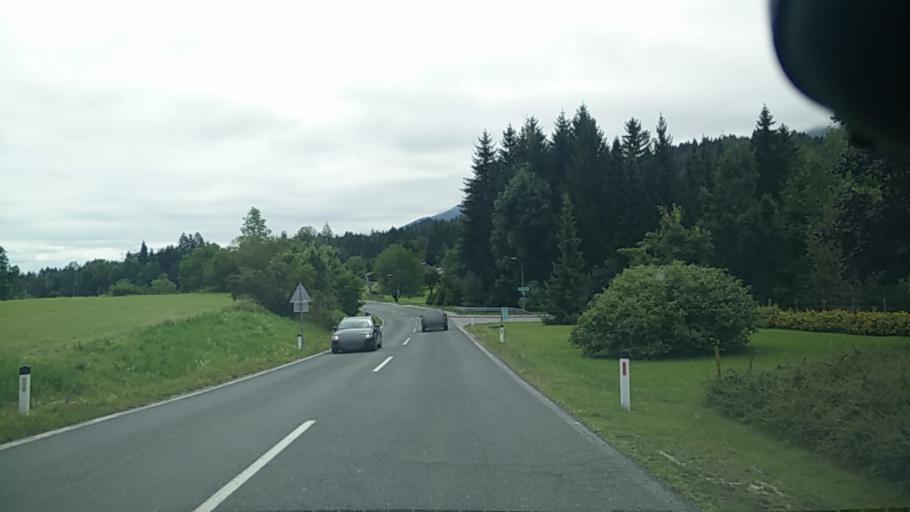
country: AT
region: Carinthia
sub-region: Politischer Bezirk Villach Land
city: Wernberg
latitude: 46.5568
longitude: 13.9492
